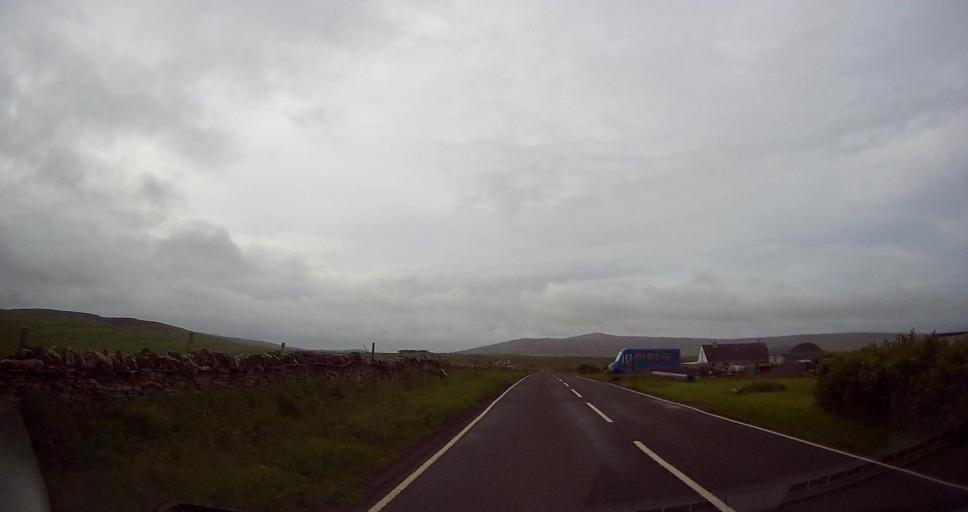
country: GB
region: Scotland
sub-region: Orkney Islands
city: Stromness
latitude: 59.0116
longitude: -3.1556
